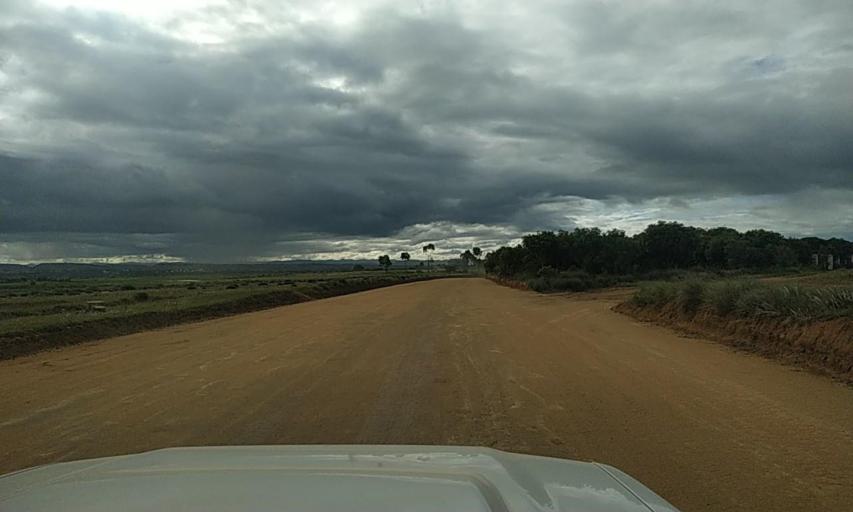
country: MG
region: Alaotra Mangoro
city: Ambatondrazaka
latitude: -17.9019
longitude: 48.2583
